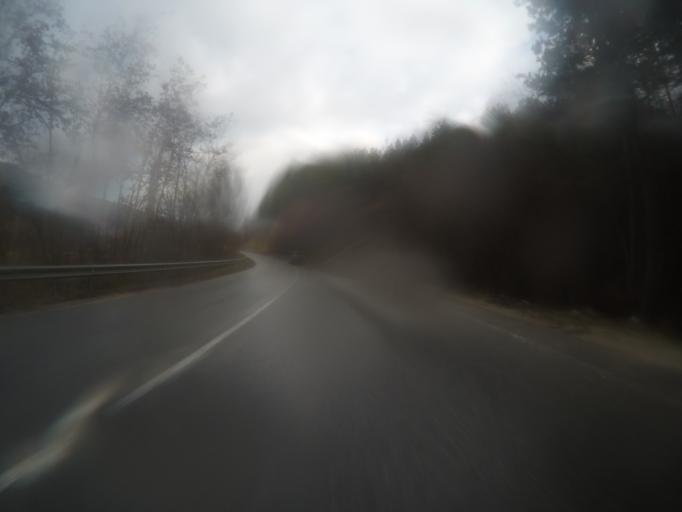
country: BG
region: Blagoevgrad
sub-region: Obshtina Simitli
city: Simitli
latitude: 41.8918
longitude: 23.1615
